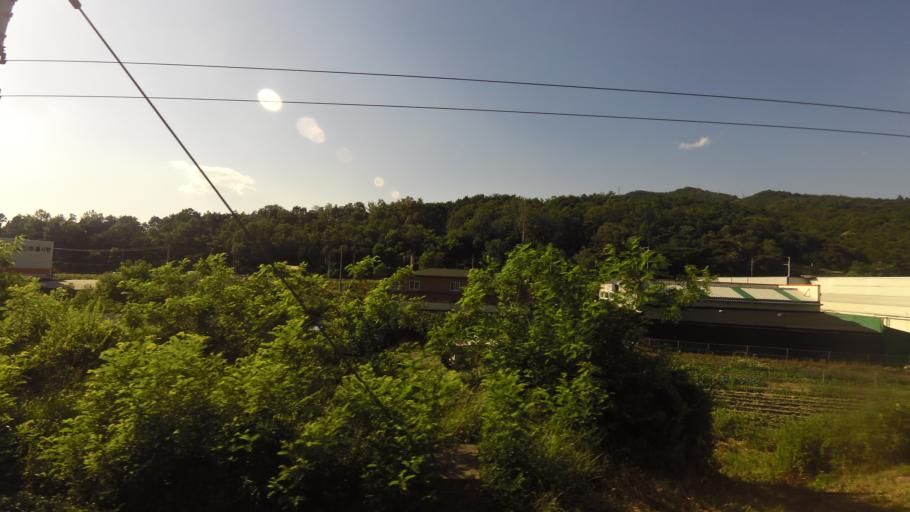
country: KR
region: Gyeongsangbuk-do
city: Waegwan
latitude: 35.9639
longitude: 128.4578
